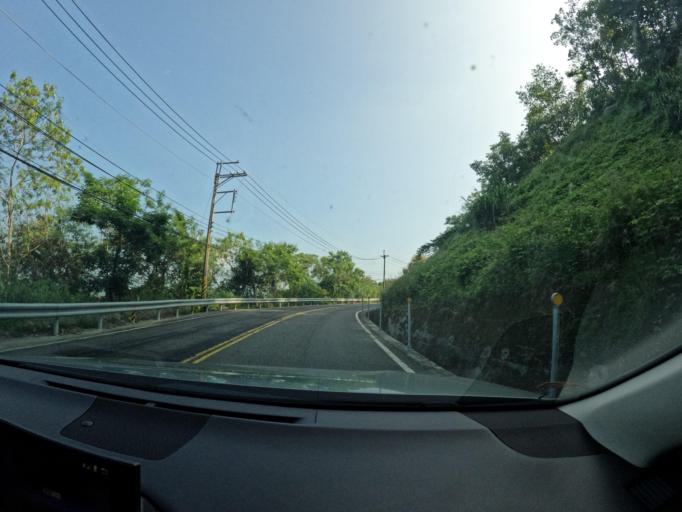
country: TW
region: Taiwan
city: Yujing
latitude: 23.0720
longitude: 120.5466
